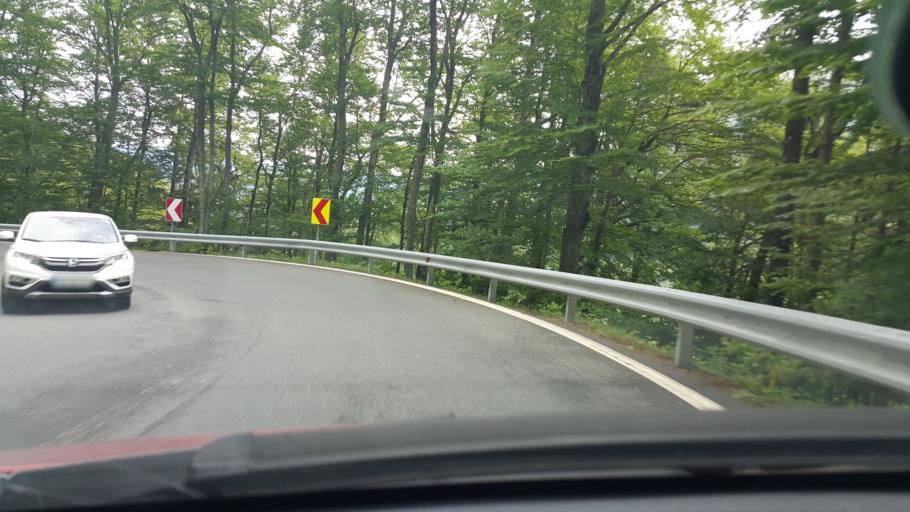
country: AT
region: Carinthia
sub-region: Politischer Bezirk Klagenfurt Land
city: Ferlach
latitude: 46.4918
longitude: 14.2795
